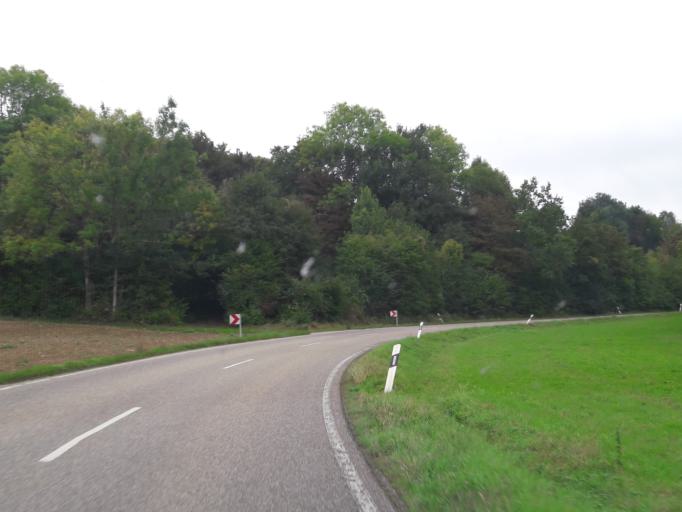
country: DE
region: Baden-Wuerttemberg
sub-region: Regierungsbezirk Stuttgart
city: Widdern
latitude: 49.3082
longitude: 9.4242
